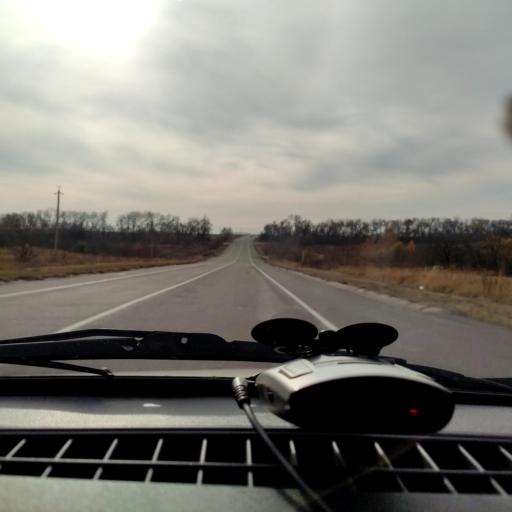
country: RU
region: Voronezj
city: Devitsa
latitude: 51.5745
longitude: 38.9748
